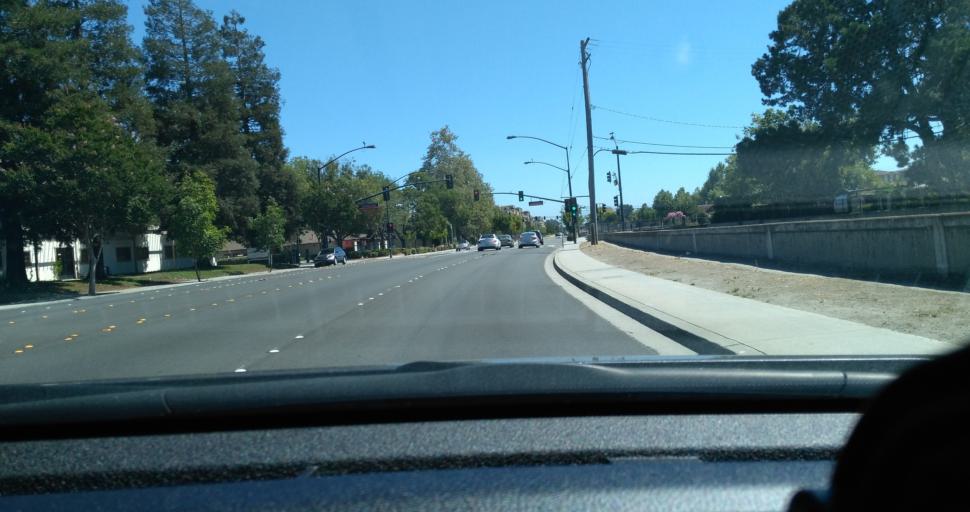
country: US
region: California
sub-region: Santa Clara County
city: Milpitas
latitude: 37.4255
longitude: -121.9076
